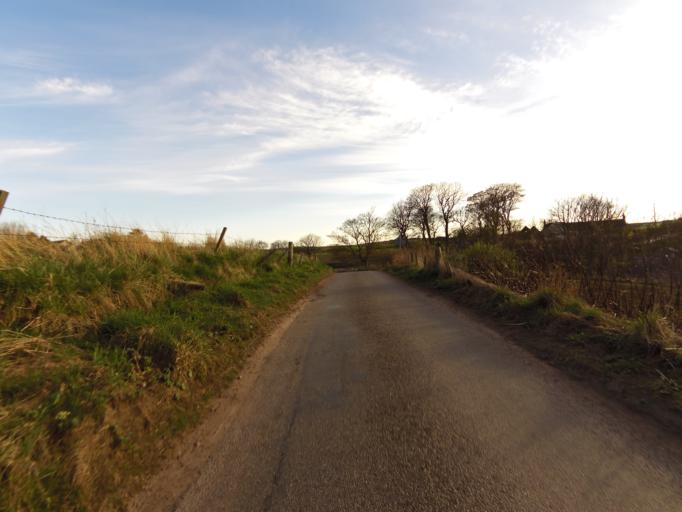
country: GB
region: Scotland
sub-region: Aberdeenshire
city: Stonehaven
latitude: 56.8983
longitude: -2.2174
